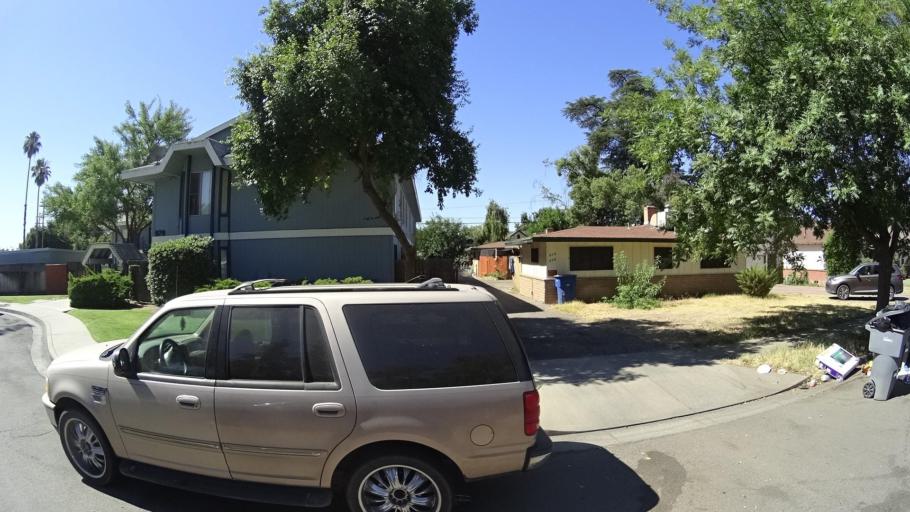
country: US
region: California
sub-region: Fresno County
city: Fresno
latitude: 36.7732
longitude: -119.7982
